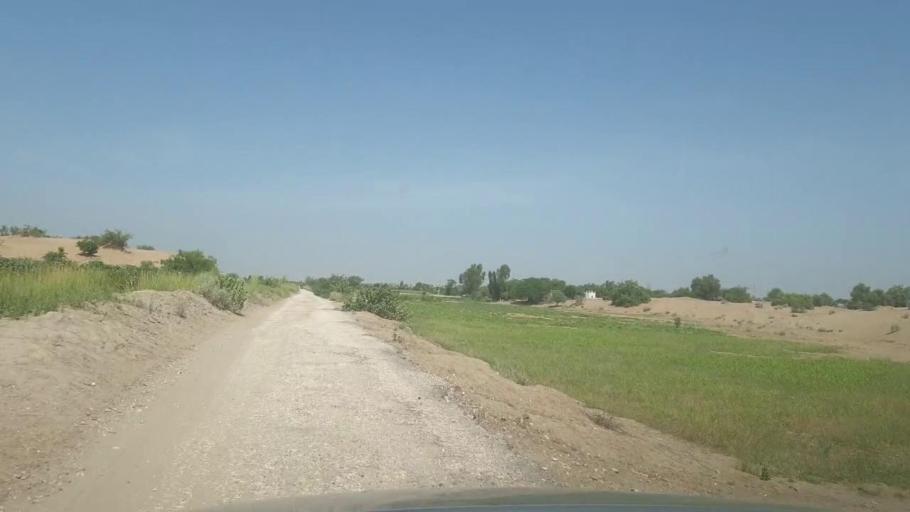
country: PK
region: Sindh
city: Khairpur
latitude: 27.3963
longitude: 69.0710
